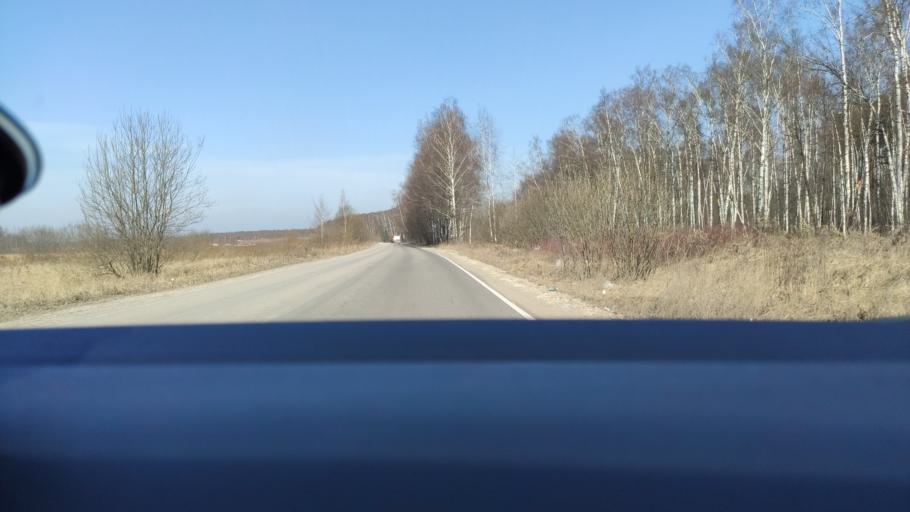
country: RU
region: Moskovskaya
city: Elektrostal'
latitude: 55.7647
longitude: 38.3873
